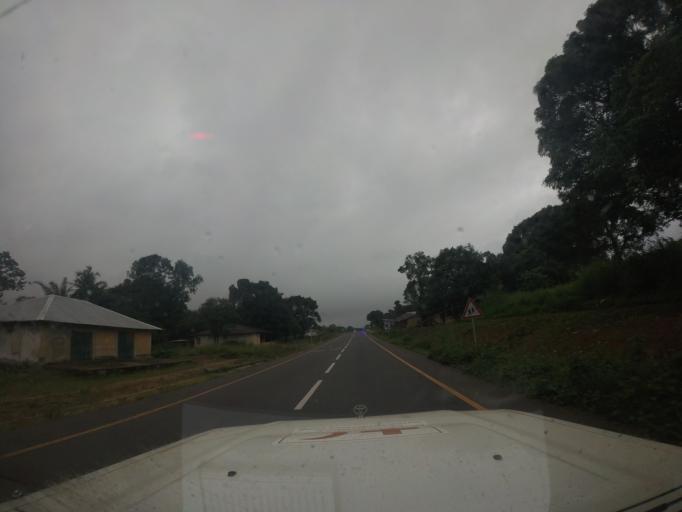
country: SL
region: Eastern Province
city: Hangha
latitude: 8.0234
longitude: -11.1070
